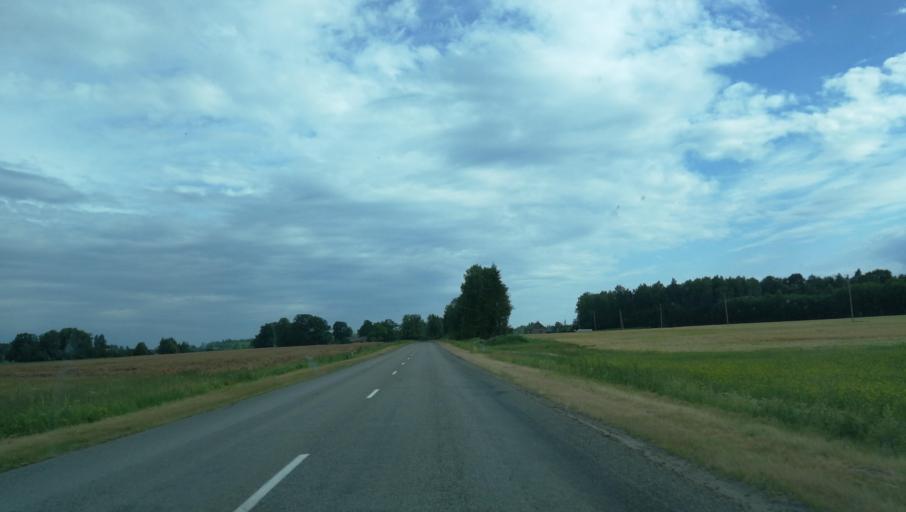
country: LV
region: Valmieras Rajons
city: Valmiera
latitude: 57.5989
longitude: 25.4592
